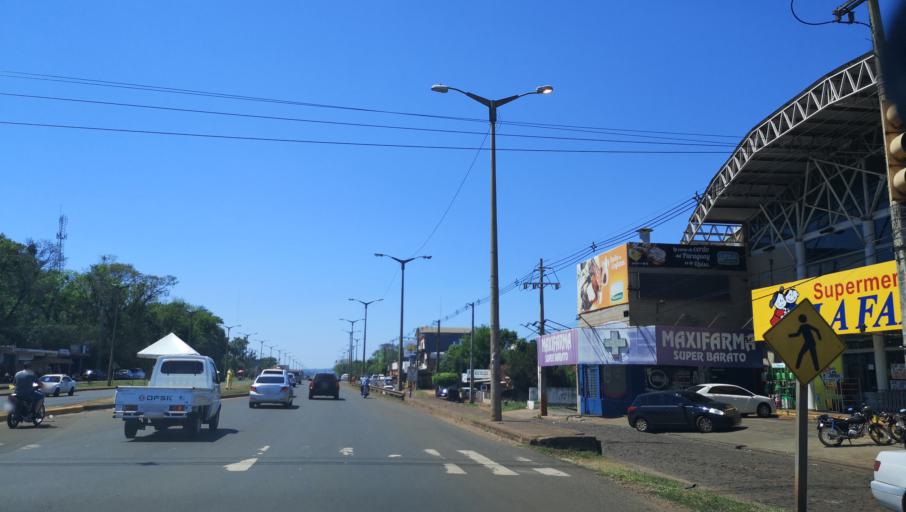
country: PY
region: Itapua
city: Encarnacion
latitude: -27.3118
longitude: -55.8832
